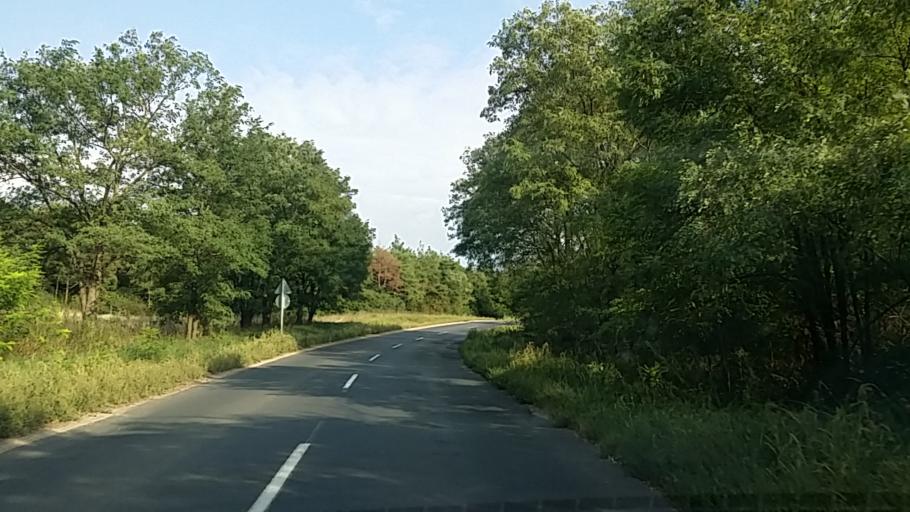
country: HU
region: Gyor-Moson-Sopron
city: Sopron
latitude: 47.6780
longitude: 16.6232
